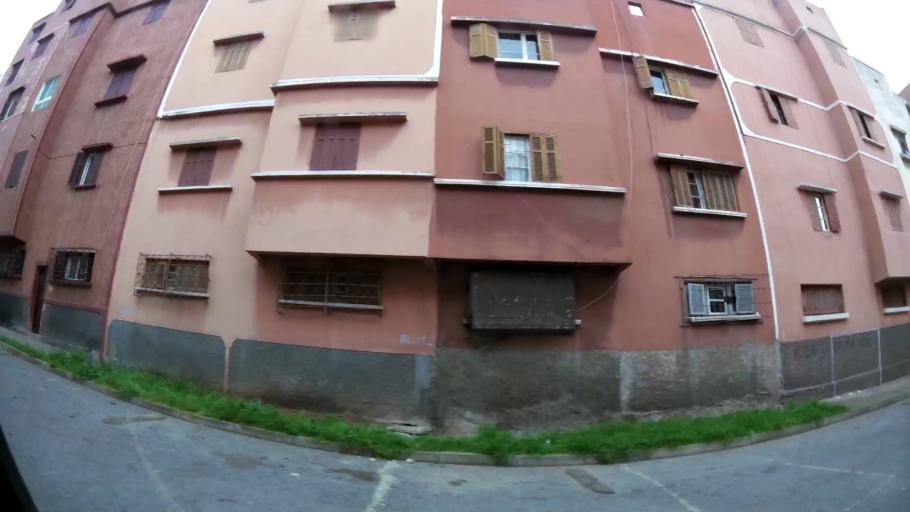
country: MA
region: Grand Casablanca
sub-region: Casablanca
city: Casablanca
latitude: 33.5659
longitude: -7.5630
